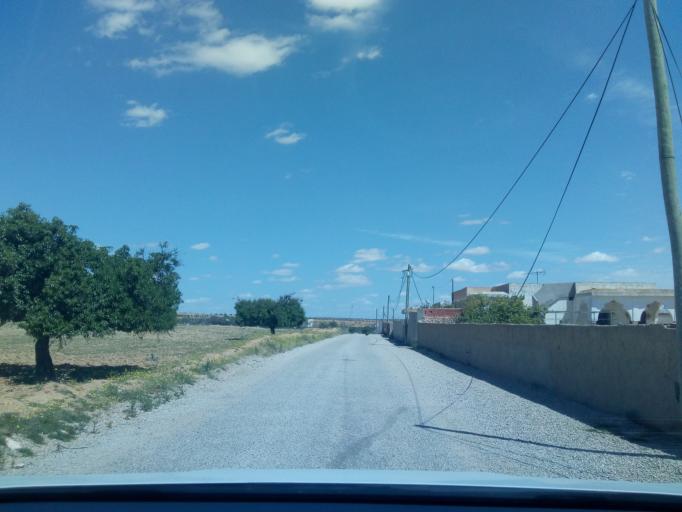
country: TN
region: Safaqis
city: Sfax
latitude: 34.7333
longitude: 10.4922
